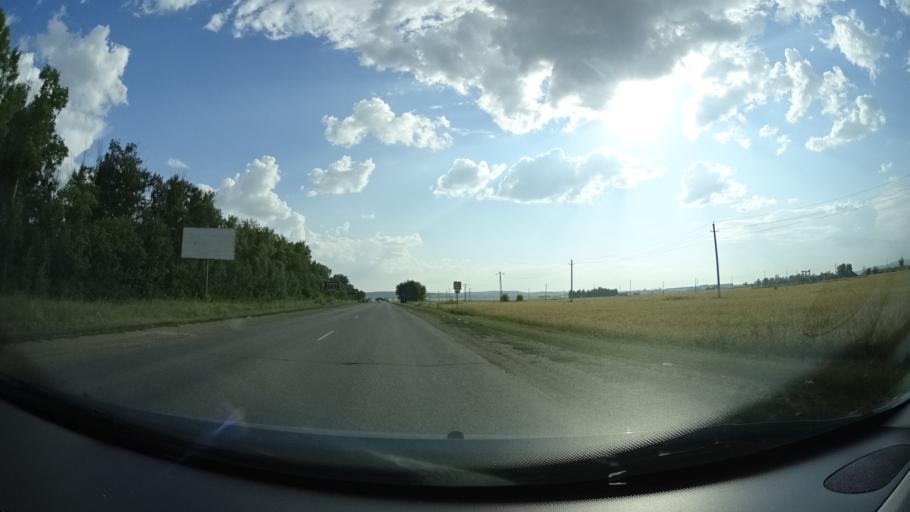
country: RU
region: Bashkortostan
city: Oktyabr'skiy
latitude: 54.4808
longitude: 53.4033
